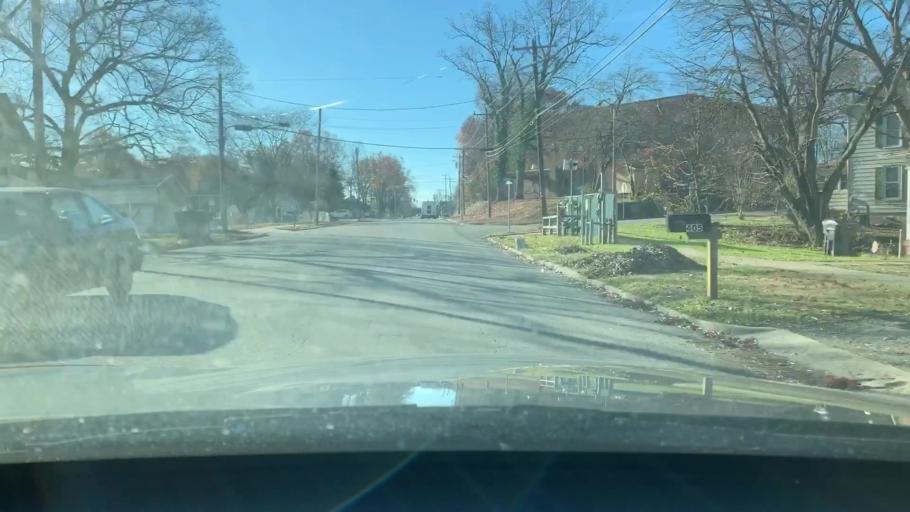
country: US
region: North Carolina
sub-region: Alamance County
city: Burlington
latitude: 36.0942
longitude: -79.4292
